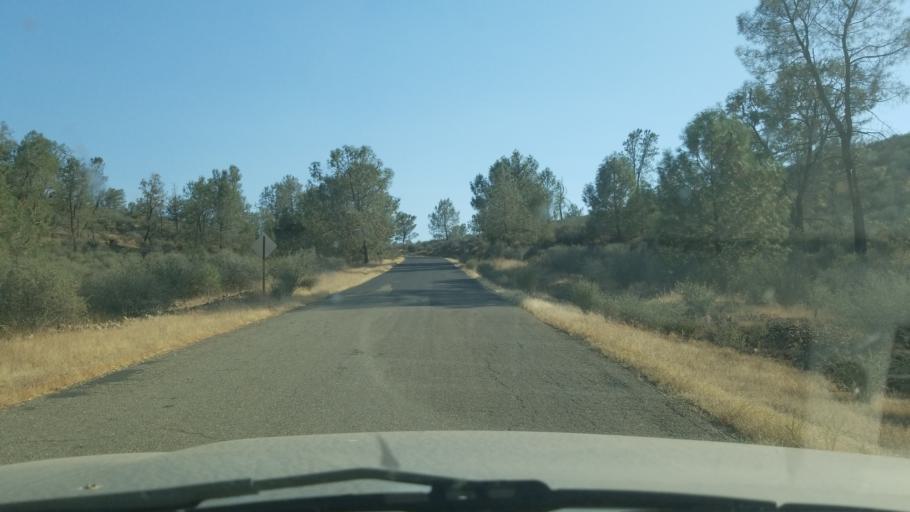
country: US
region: California
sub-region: Tuolumne County
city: Jamestown
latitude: 37.8384
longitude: -120.4702
